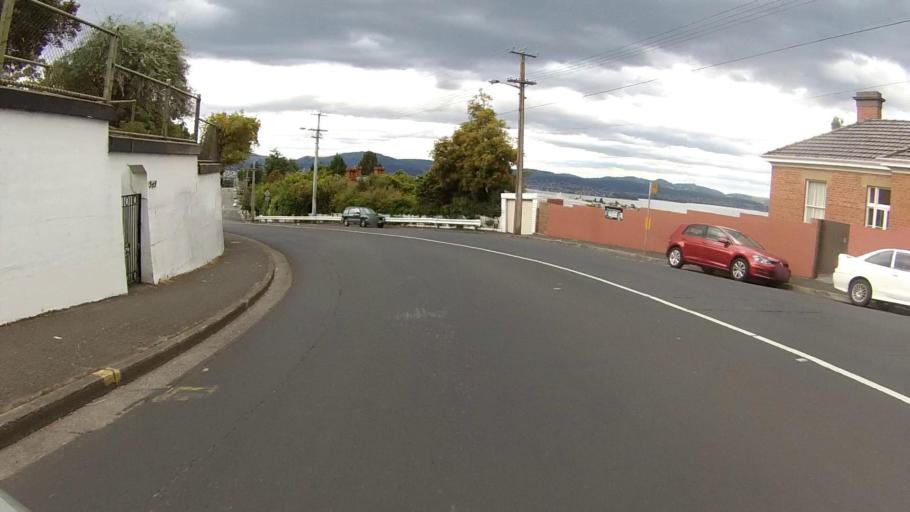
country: AU
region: Tasmania
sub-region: Hobart
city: Dynnyrne
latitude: -42.8994
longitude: 147.3123
